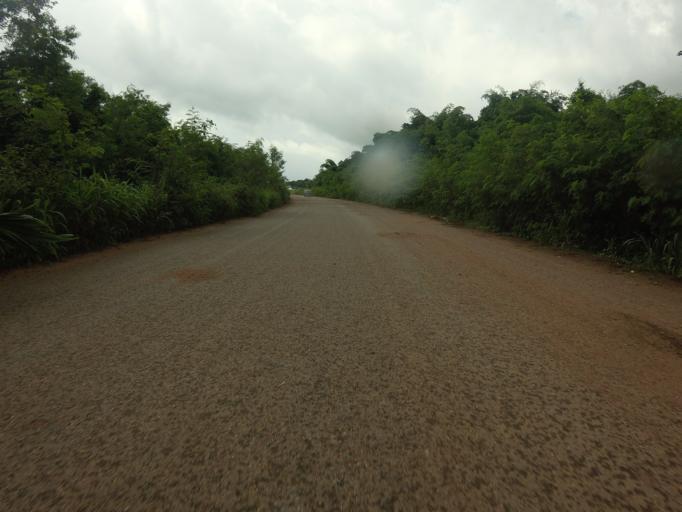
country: TG
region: Plateaux
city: Kpalime
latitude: 6.9310
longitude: 0.4626
